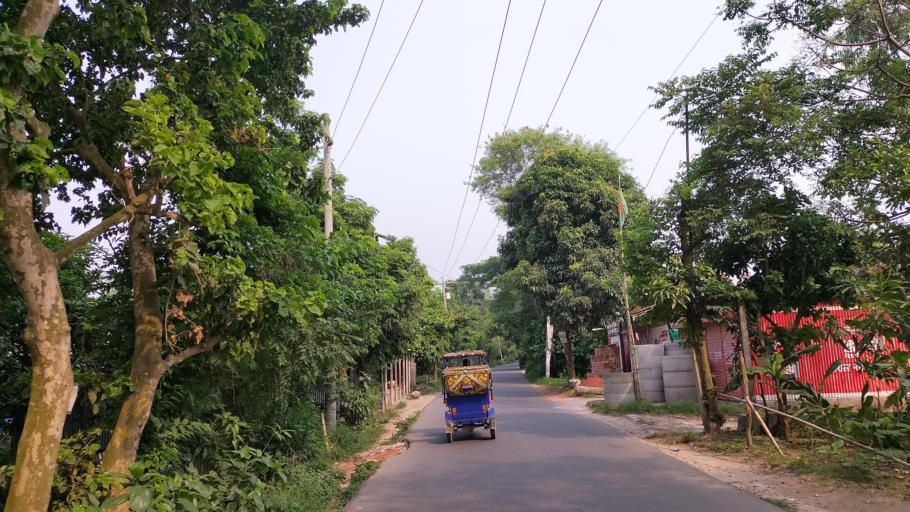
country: BD
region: Dhaka
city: Azimpur
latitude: 23.6785
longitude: 90.3155
